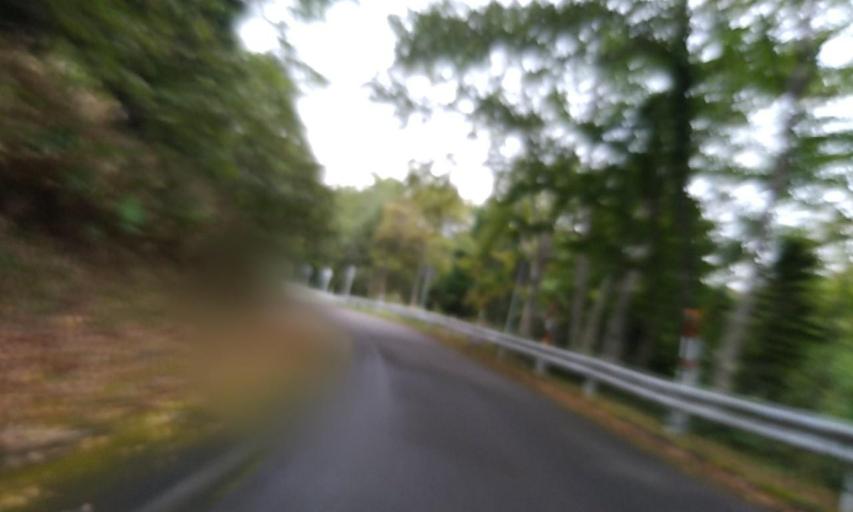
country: JP
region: Hokkaido
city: Bihoro
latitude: 43.5704
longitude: 144.1949
